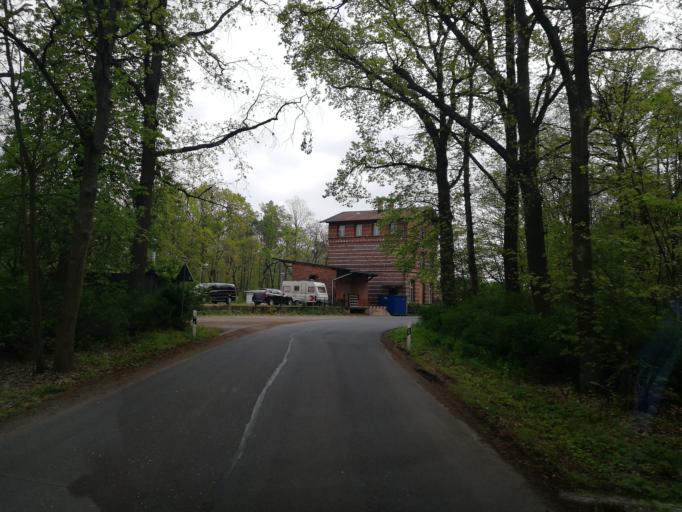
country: DE
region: Brandenburg
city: Herzberg
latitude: 51.6431
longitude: 13.1725
